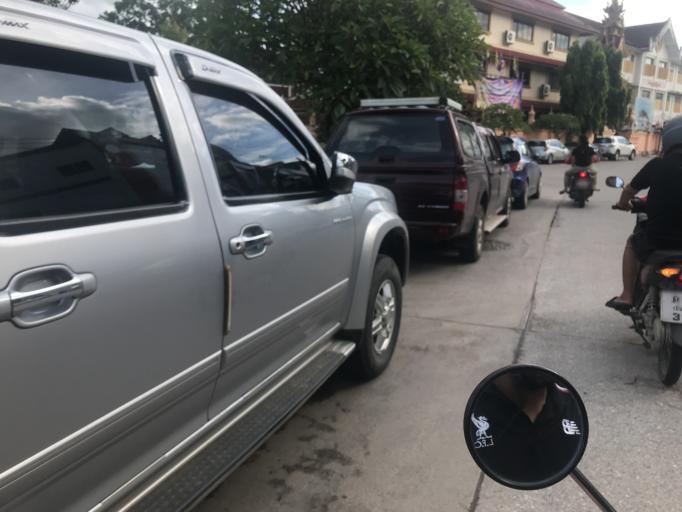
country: TH
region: Chiang Rai
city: Chiang Rai
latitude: 19.9123
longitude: 99.8312
